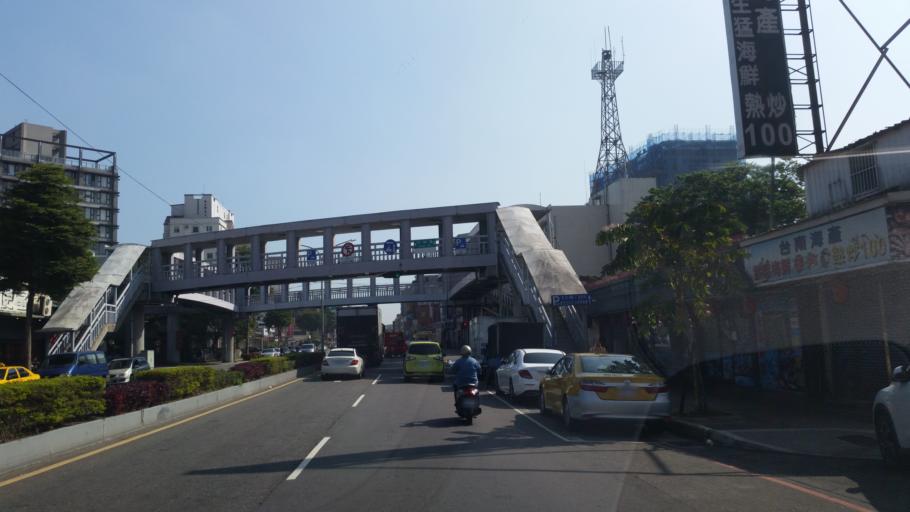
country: TW
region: Taipei
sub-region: Taipei
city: Banqiao
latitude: 25.0791
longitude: 121.3876
